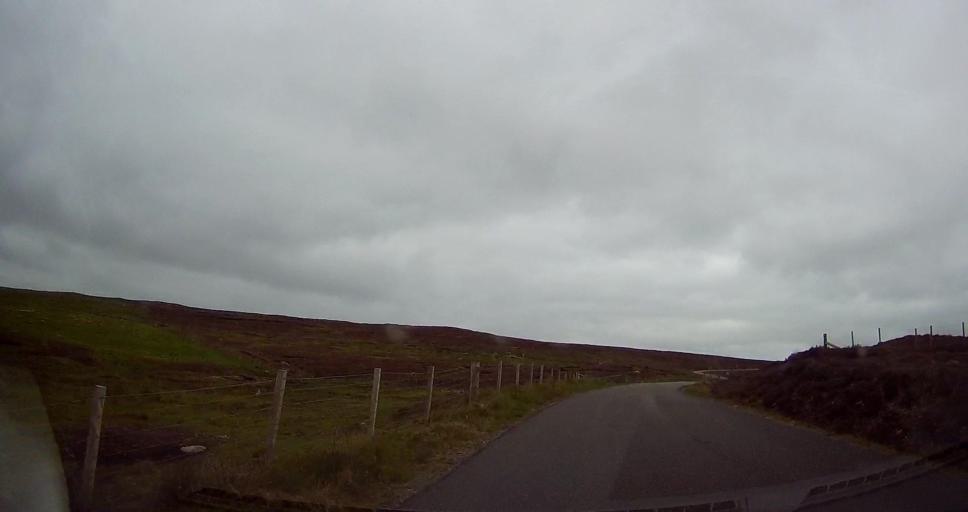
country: GB
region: Scotland
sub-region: Shetland Islands
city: Lerwick
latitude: 60.3105
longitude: -1.3381
